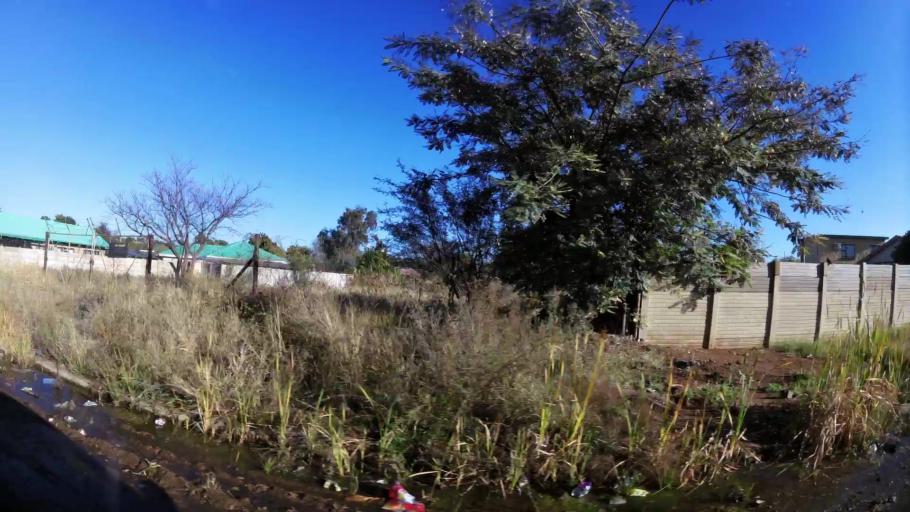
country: ZA
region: Northern Cape
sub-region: Frances Baard District Municipality
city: Kimberley
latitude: -28.7407
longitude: 24.7387
